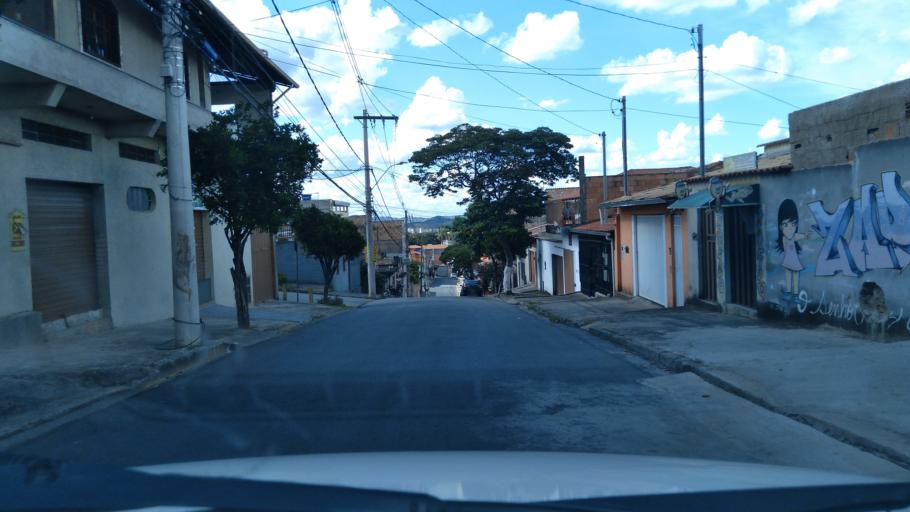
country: BR
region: Minas Gerais
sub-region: Belo Horizonte
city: Belo Horizonte
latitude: -19.8588
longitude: -43.8819
